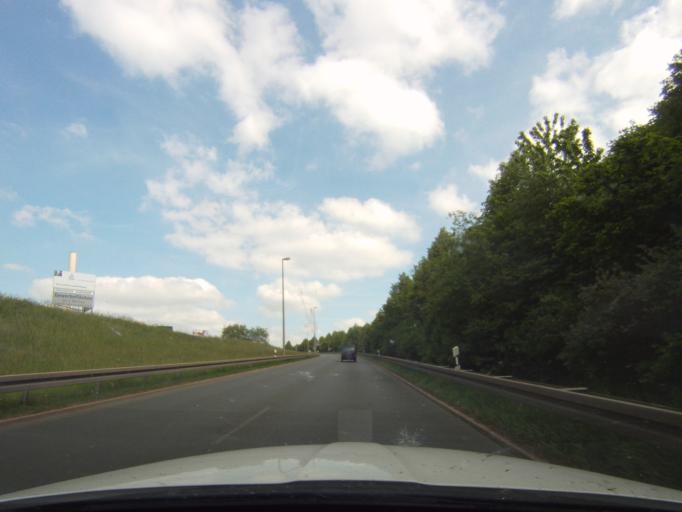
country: DE
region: Thuringia
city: Gera
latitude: 50.8609
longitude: 12.0985
